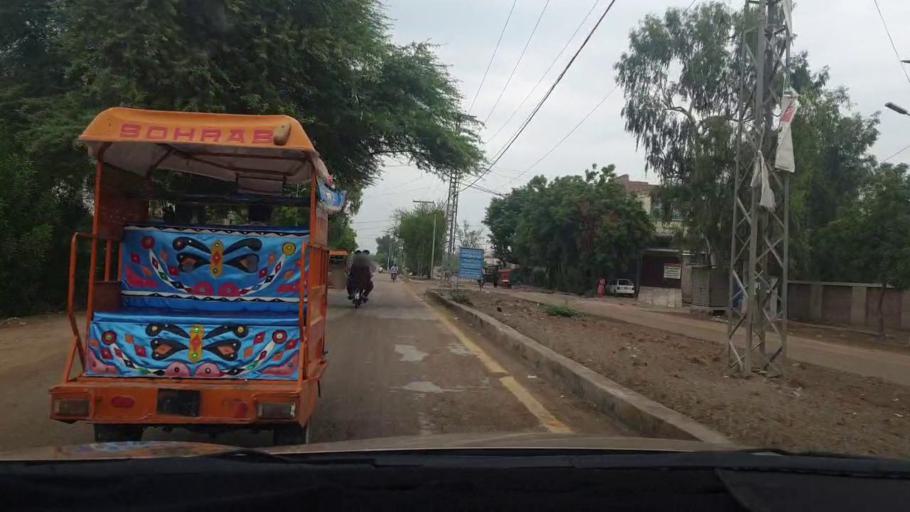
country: PK
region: Sindh
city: Larkana
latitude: 27.5627
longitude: 68.1974
